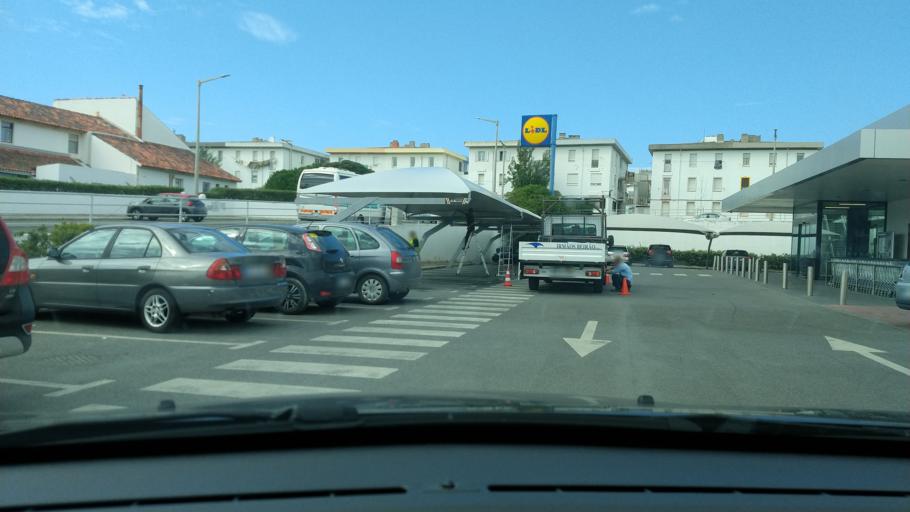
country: PT
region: Leiria
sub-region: Peniche
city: Peniche
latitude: 39.3653
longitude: -9.3804
